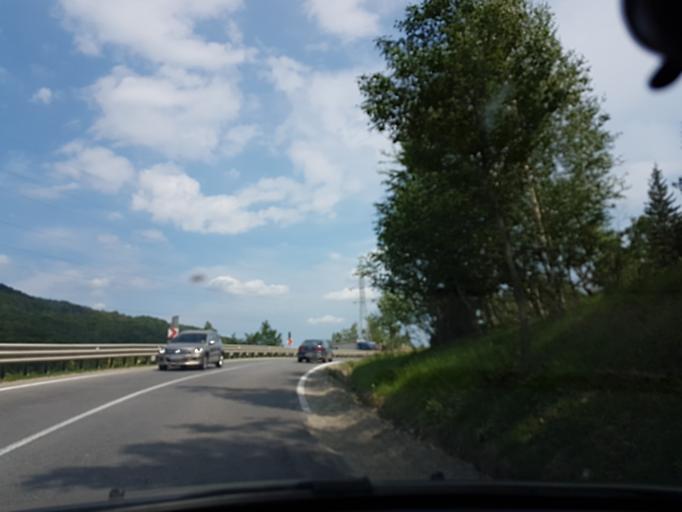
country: RO
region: Prahova
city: Maneciu
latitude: 45.3410
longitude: 25.9553
